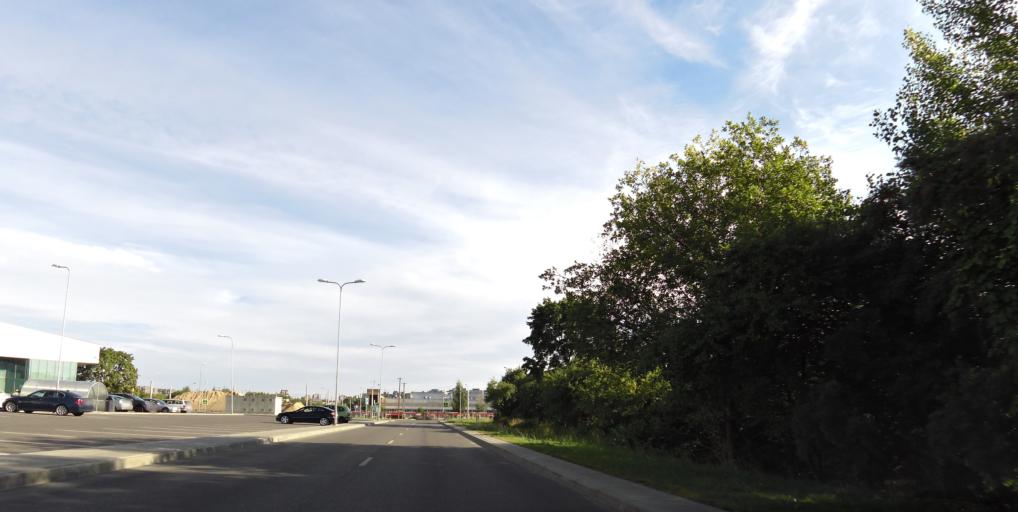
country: LT
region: Vilnius County
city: Justiniskes
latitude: 54.7016
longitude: 25.2137
